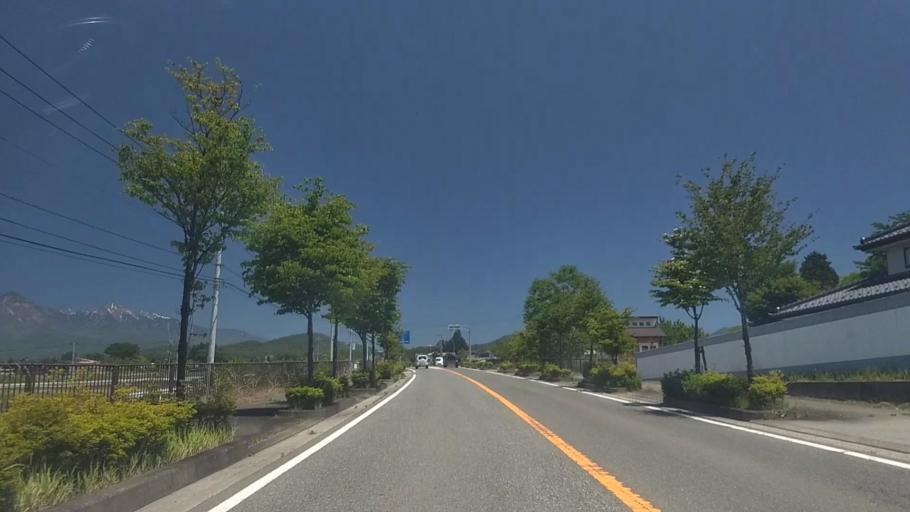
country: JP
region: Yamanashi
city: Nirasaki
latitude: 35.8283
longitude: 138.4296
